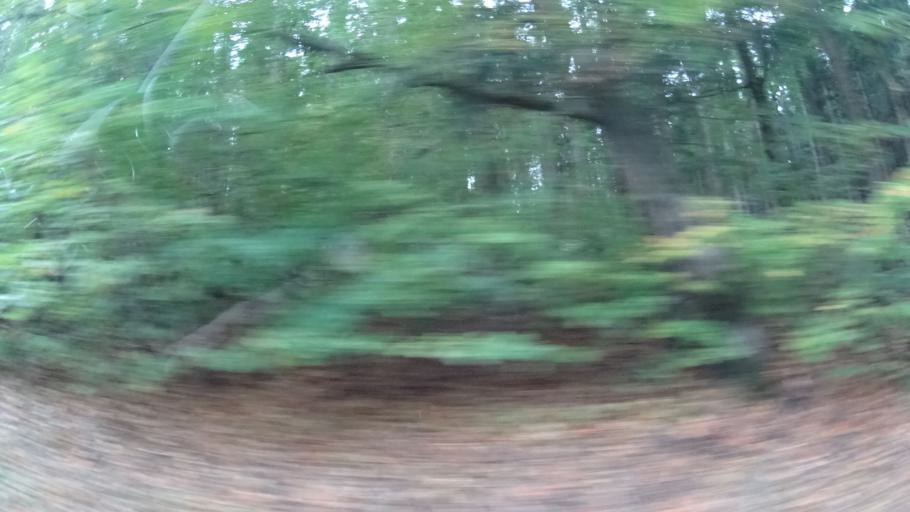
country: DE
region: Thuringia
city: Altersbach
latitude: 50.7206
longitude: 10.5270
